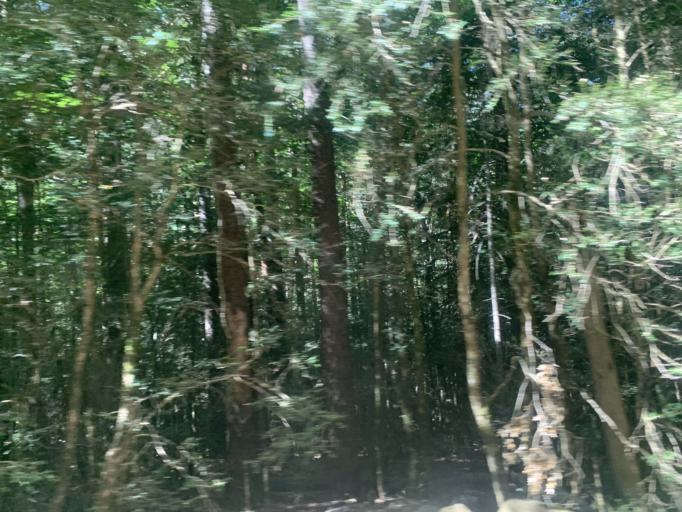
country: ES
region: Aragon
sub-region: Provincia de Huesca
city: Broto
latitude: 42.6540
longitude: -0.0783
